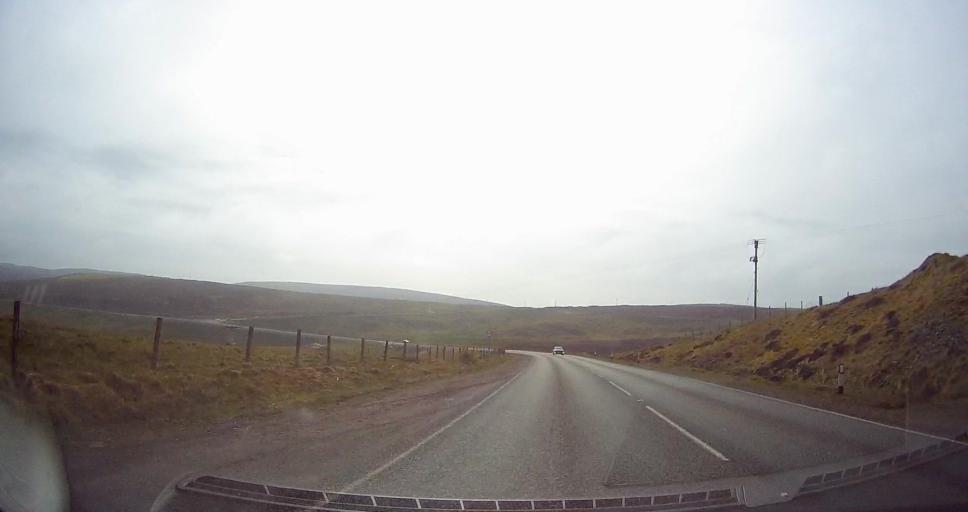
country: GB
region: Scotland
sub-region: Shetland Islands
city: Lerwick
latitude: 60.1395
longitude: -1.2052
